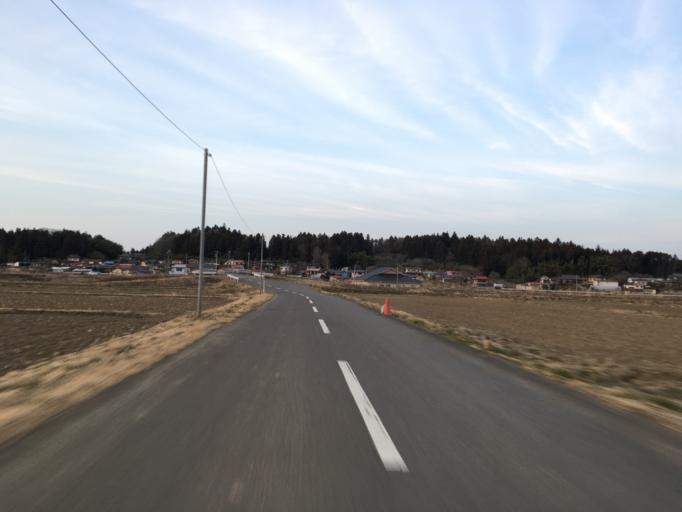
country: JP
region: Fukushima
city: Ishikawa
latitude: 37.0616
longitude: 140.3485
